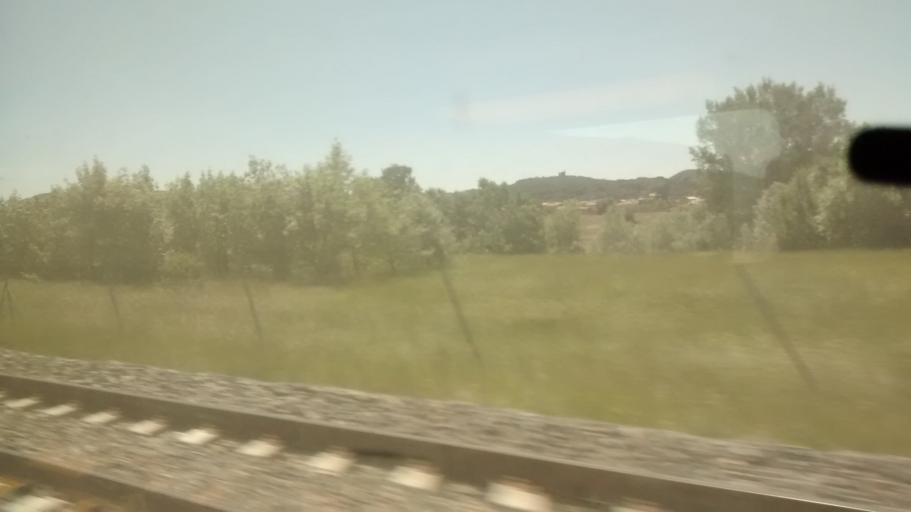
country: FR
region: Provence-Alpes-Cote d'Azur
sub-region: Departement du Vaucluse
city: Mornas
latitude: 44.1916
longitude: 4.7124
